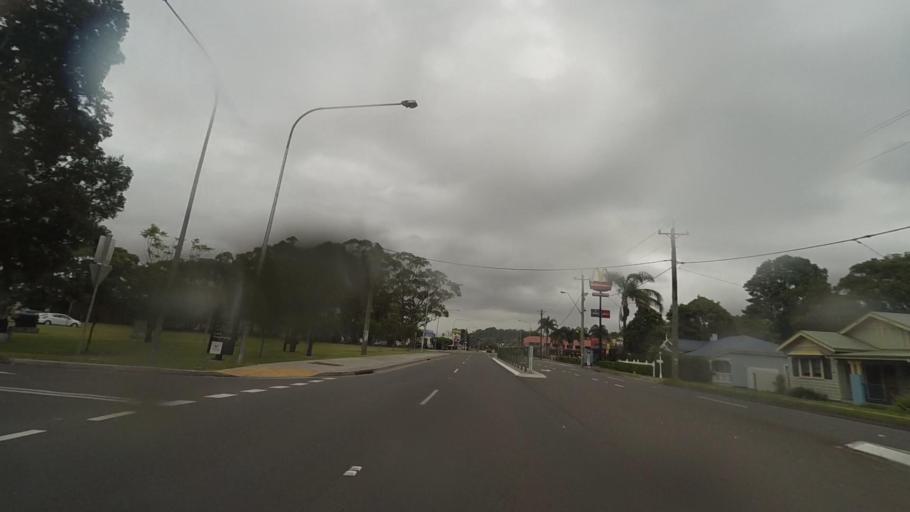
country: AU
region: New South Wales
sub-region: Wollongong
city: Mangerton
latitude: -34.4341
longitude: 150.8632
